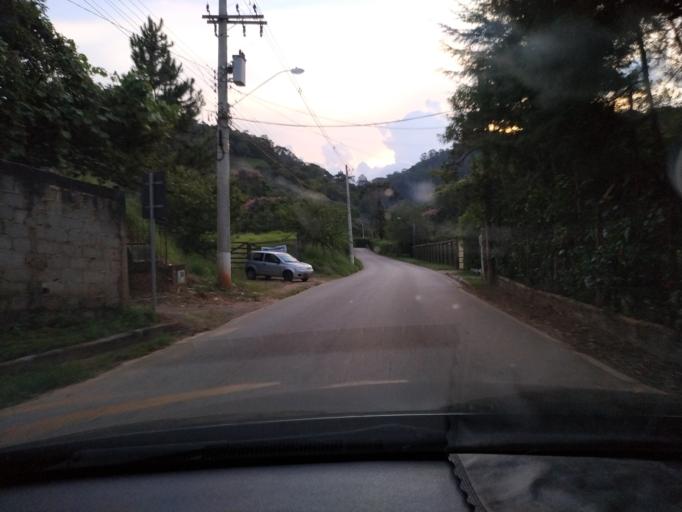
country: BR
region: Sao Paulo
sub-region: Campos Do Jordao
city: Campos do Jordao
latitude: -22.8139
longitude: -45.6602
